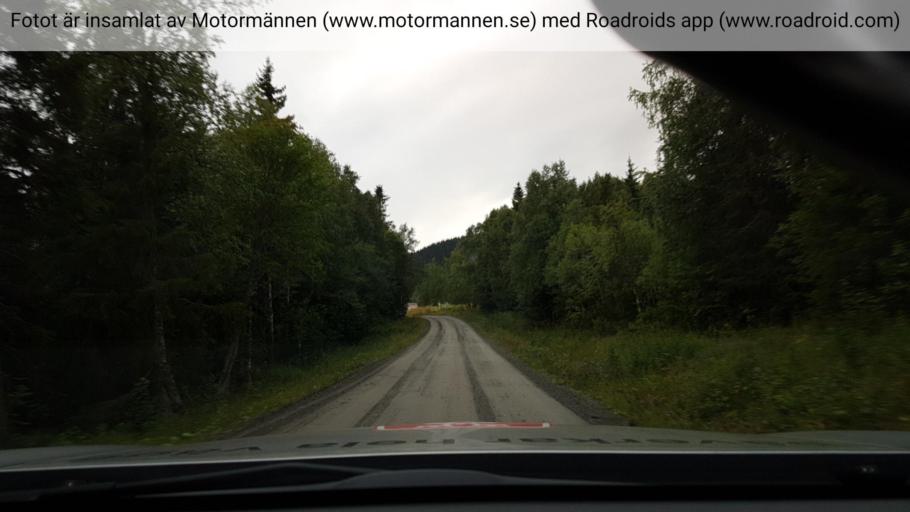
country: NO
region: Nordland
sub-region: Hattfjelldal
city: Hattfjelldal
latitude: 65.6585
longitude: 15.1496
